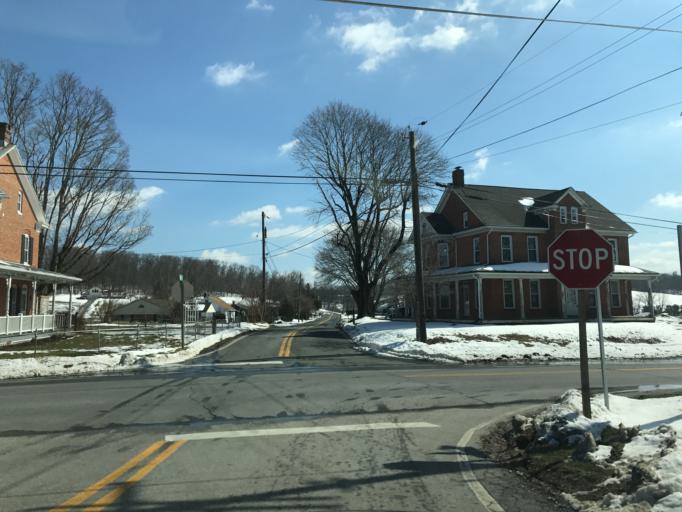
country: US
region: Maryland
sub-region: Carroll County
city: Manchester
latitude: 39.7161
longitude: -76.8497
